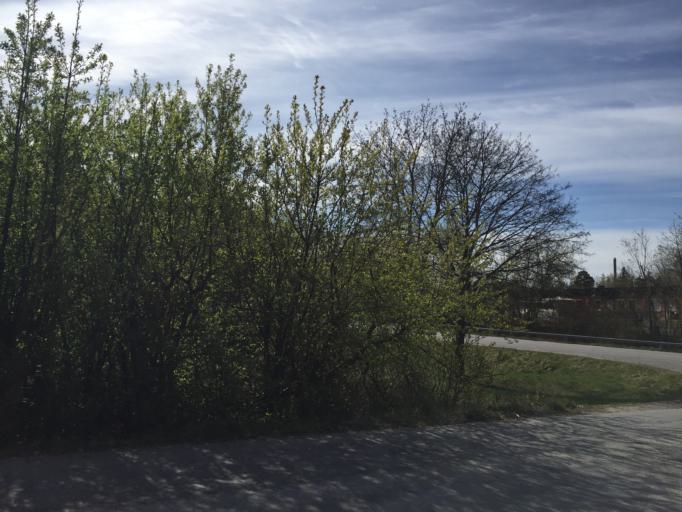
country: SE
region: Stockholm
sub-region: Salems Kommun
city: Ronninge
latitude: 59.2092
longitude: 17.7618
